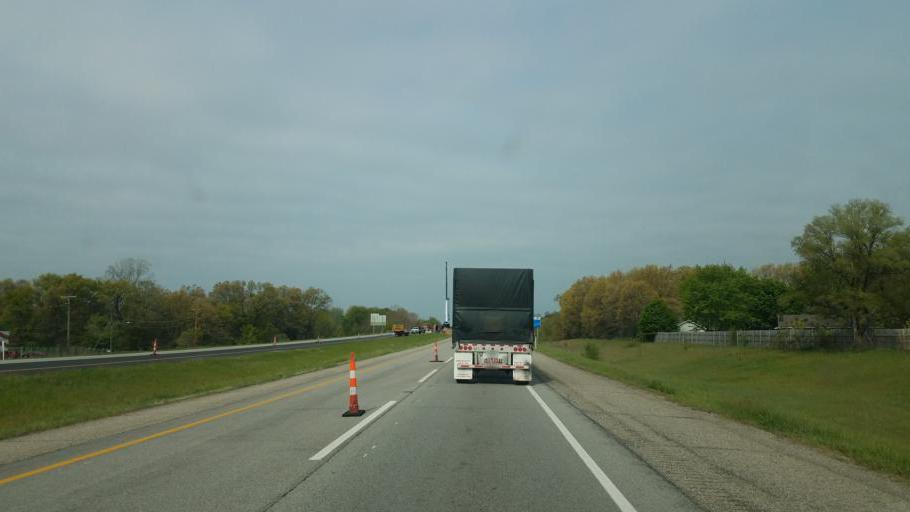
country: US
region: Indiana
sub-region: Elkhart County
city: Simonton Lake
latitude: 41.7313
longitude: -85.9796
